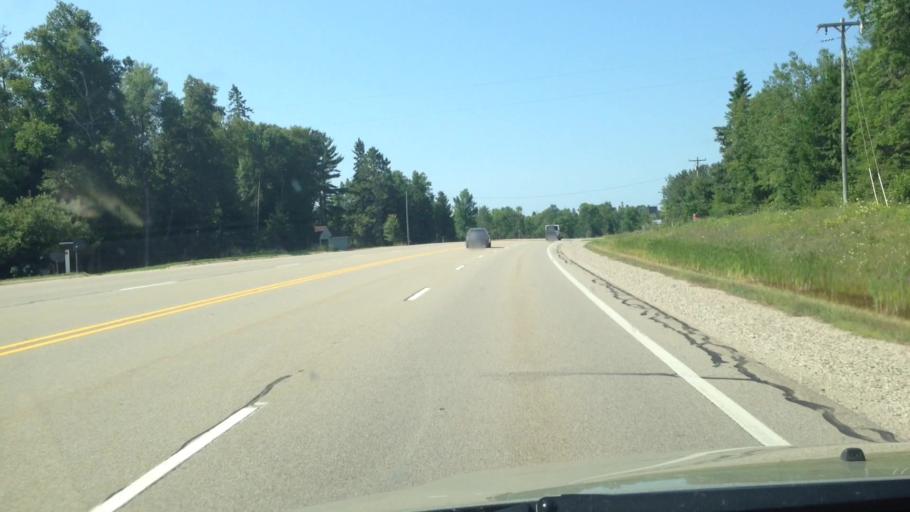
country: US
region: Michigan
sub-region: Delta County
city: Escanaba
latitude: 45.5460
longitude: -87.2721
